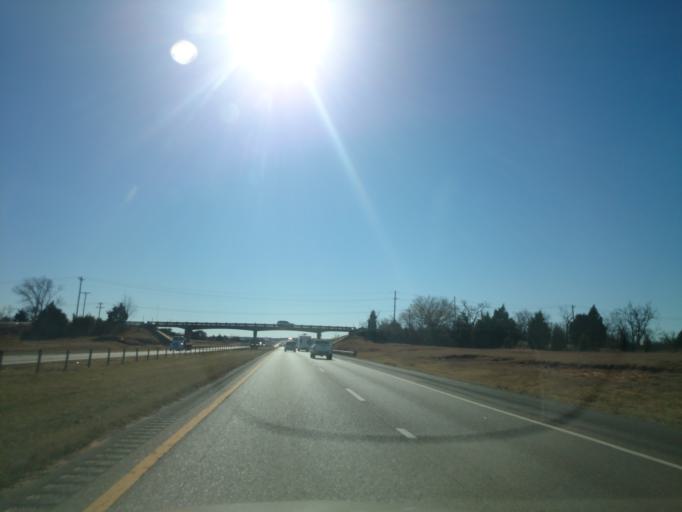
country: US
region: Oklahoma
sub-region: Oklahoma County
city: Edmond
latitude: 35.7121
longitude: -97.4163
